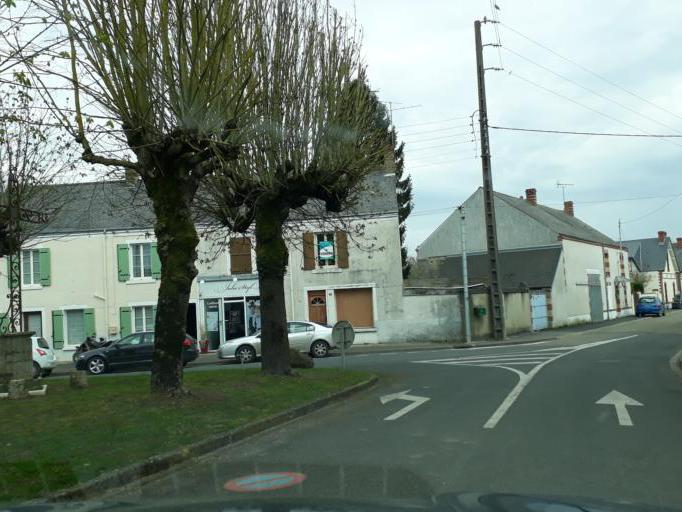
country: FR
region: Centre
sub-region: Departement du Loiret
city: Epieds-en-Beauce
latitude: 47.9466
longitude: 1.6203
